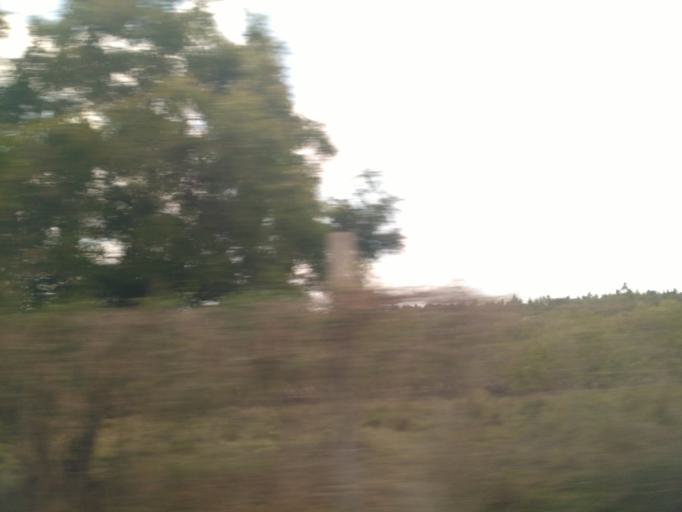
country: TZ
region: Dar es Salaam
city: Dar es Salaam
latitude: -6.8559
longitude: 39.3617
